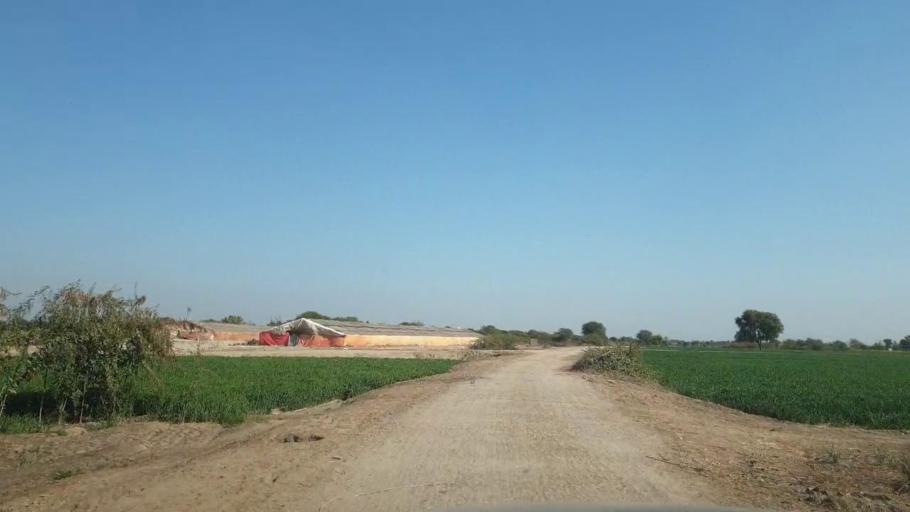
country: PK
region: Sindh
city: Tando Adam
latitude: 25.6721
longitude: 68.6872
